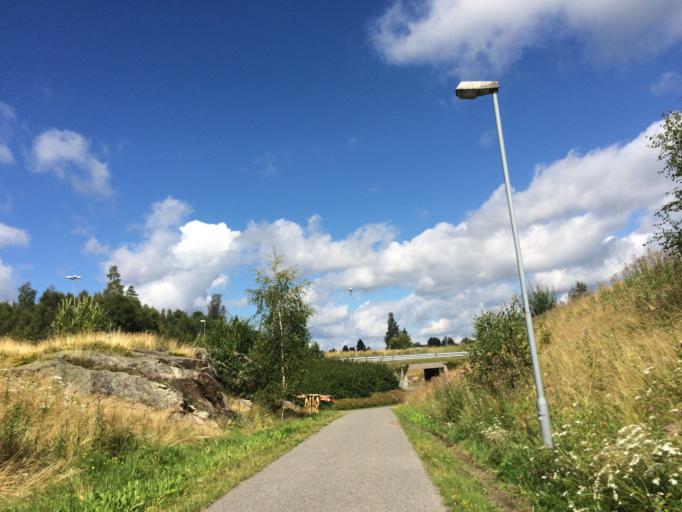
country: NO
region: Akershus
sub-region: Ski
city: Ski
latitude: 59.7115
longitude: 10.8305
